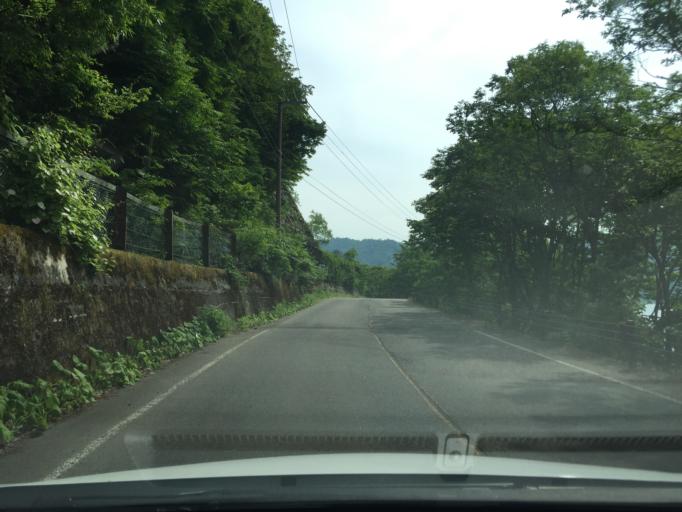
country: JP
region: Fukushima
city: Inawashiro
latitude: 37.7209
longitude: 140.0589
